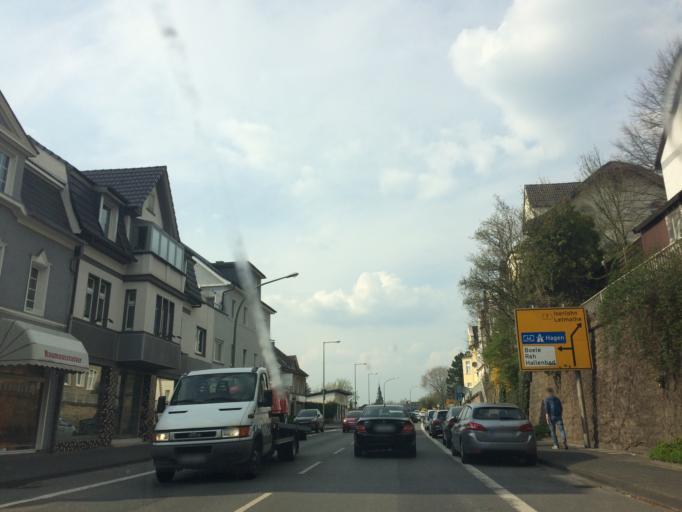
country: DE
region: North Rhine-Westphalia
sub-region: Regierungsbezirk Arnsberg
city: Nachrodt-Wiblingwerde
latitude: 51.3556
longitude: 7.5646
